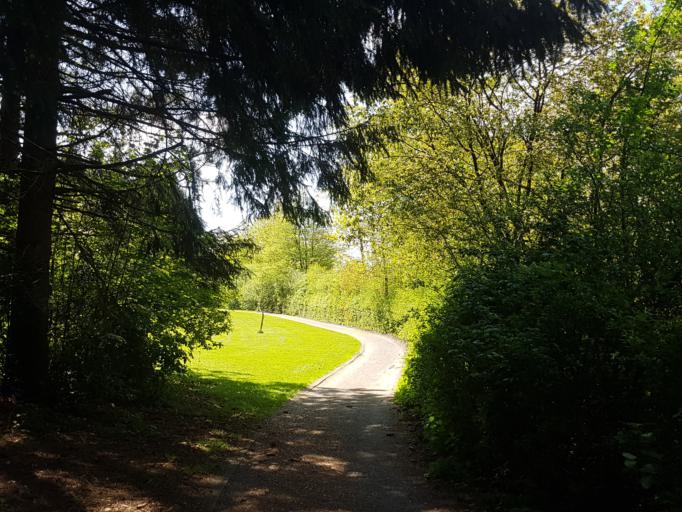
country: DE
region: North Rhine-Westphalia
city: Waldbrol
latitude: 50.8780
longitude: 7.6324
